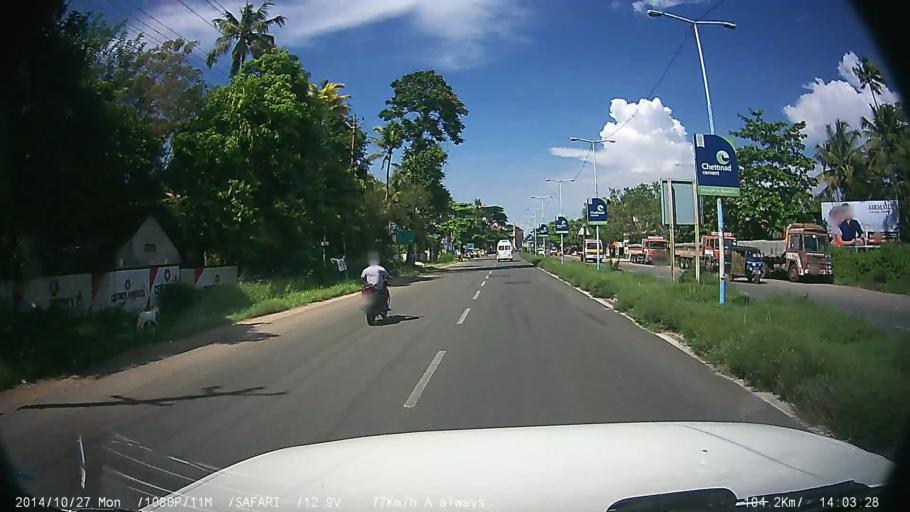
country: IN
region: Kerala
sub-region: Alappuzha
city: Vayalar
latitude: 9.7217
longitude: 76.3179
